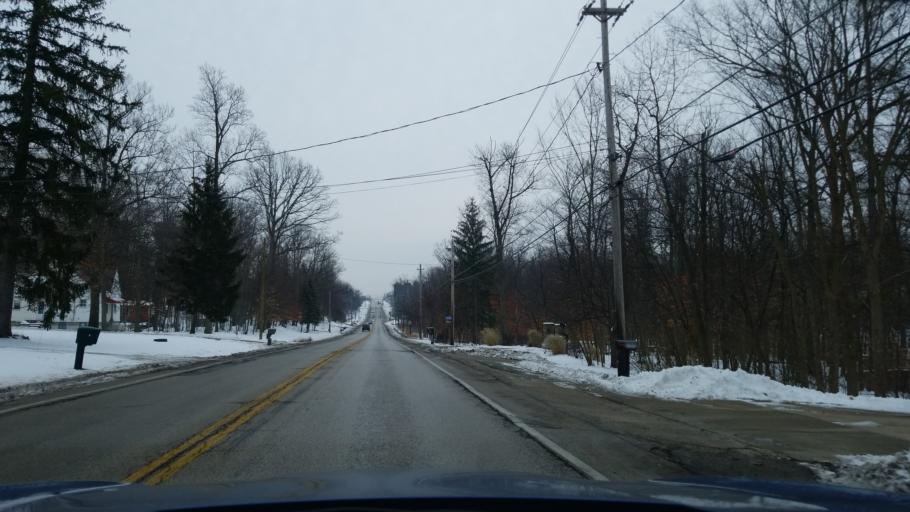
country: US
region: Ohio
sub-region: Cuyahoga County
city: Broadview Heights
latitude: 41.3138
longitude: -81.6990
